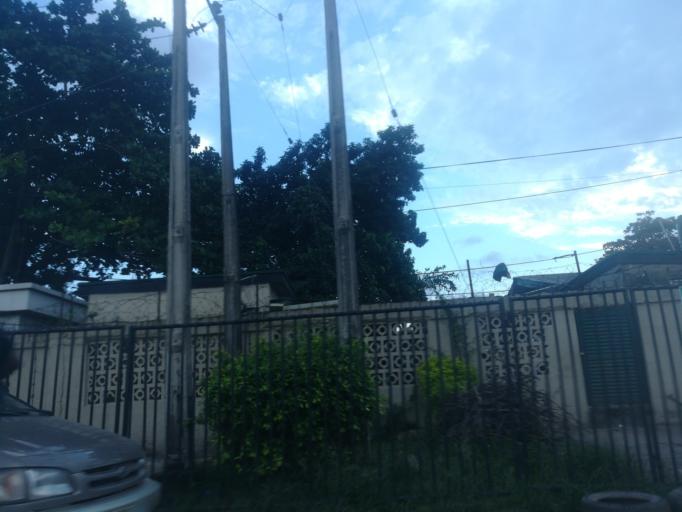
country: NG
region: Lagos
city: Somolu
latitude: 6.5533
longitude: 3.3783
